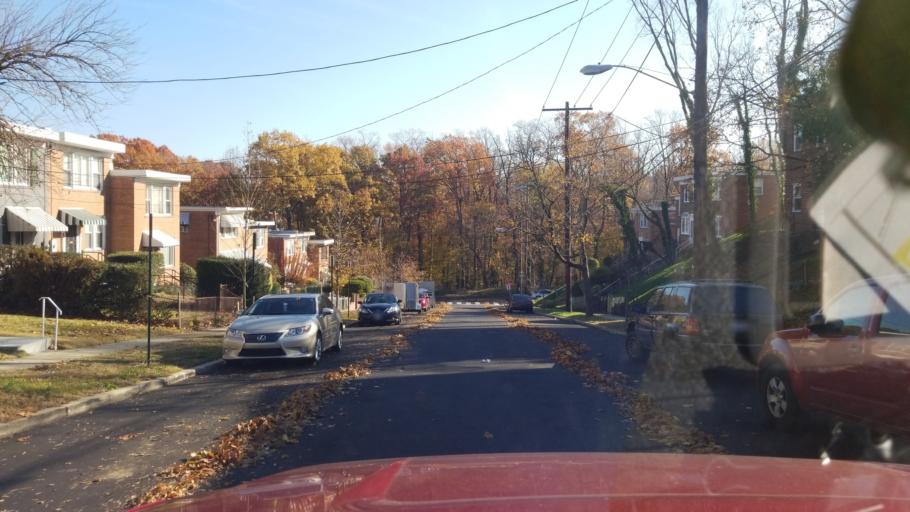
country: US
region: Maryland
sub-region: Prince George's County
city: Coral Hills
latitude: 38.8838
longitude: -76.9464
